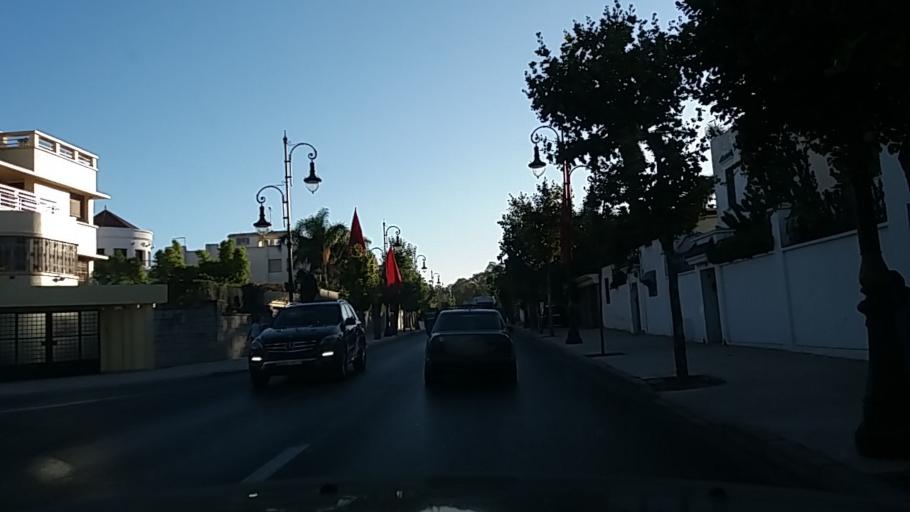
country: MA
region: Tanger-Tetouan
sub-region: Tanger-Assilah
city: Tangier
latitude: 35.7797
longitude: -5.8290
